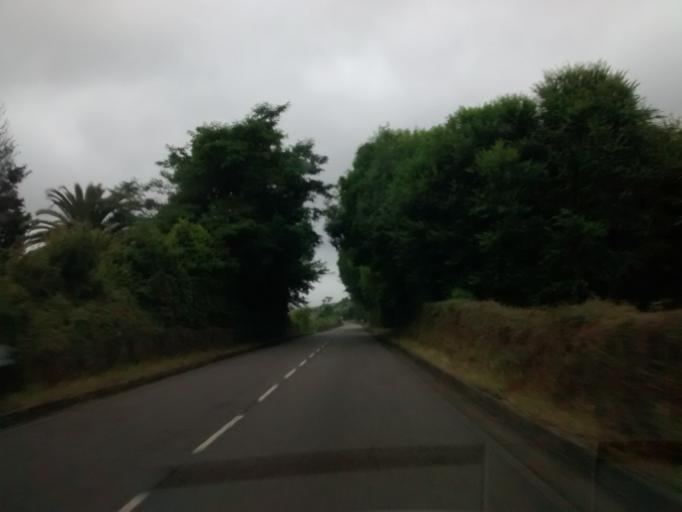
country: ES
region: Asturias
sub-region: Province of Asturias
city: Villaviciosa
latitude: 43.5072
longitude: -5.4221
